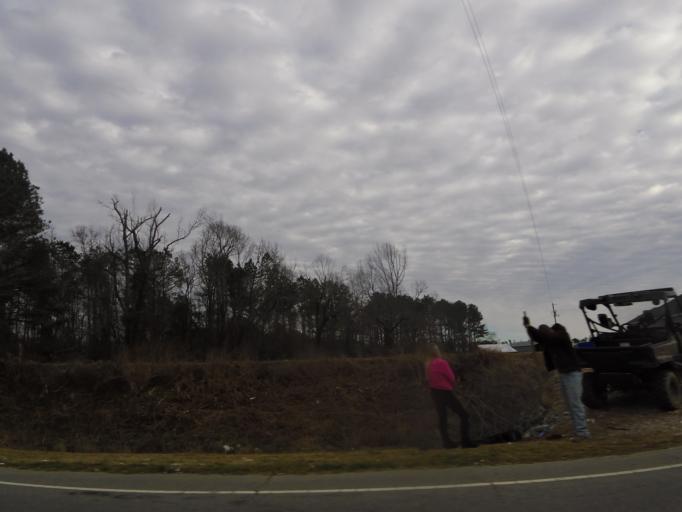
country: US
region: North Carolina
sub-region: Hertford County
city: Murfreesboro
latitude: 36.4030
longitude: -77.1521
